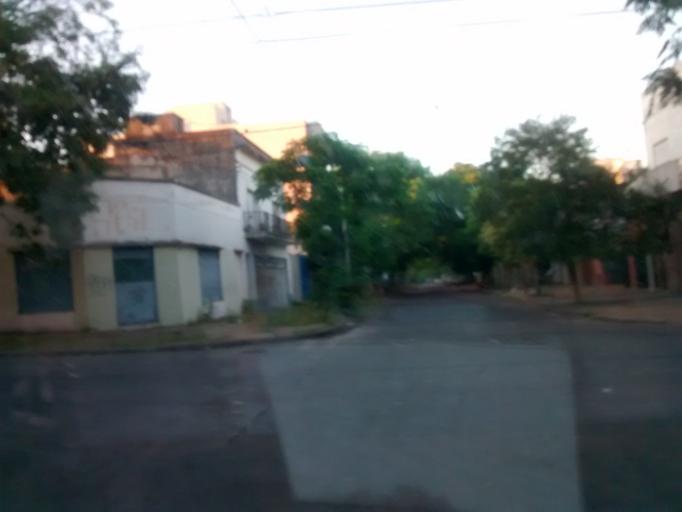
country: AR
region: Buenos Aires
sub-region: Partido de La Plata
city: La Plata
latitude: -34.9417
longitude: -57.9477
